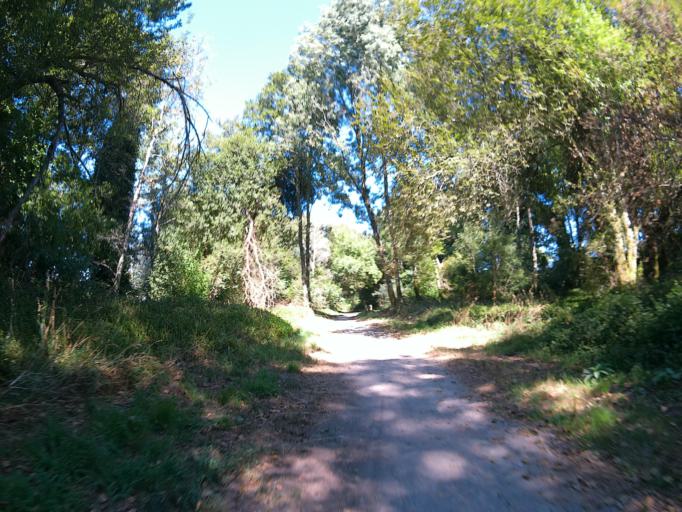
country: PT
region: Viana do Castelo
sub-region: Ponte de Lima
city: Ponte de Lima
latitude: 41.7613
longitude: -8.5969
